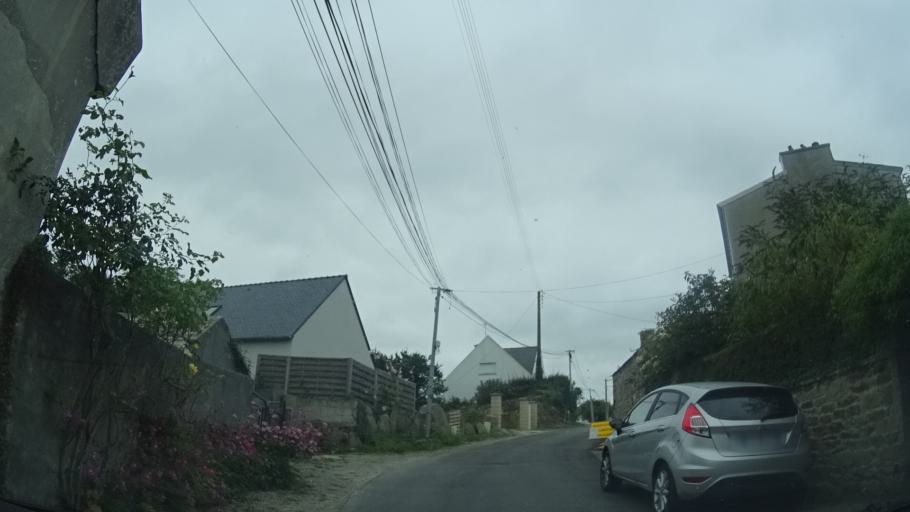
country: FR
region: Brittany
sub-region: Departement du Finistere
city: Lampaul-Plouarzel
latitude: 48.4502
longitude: -4.7601
